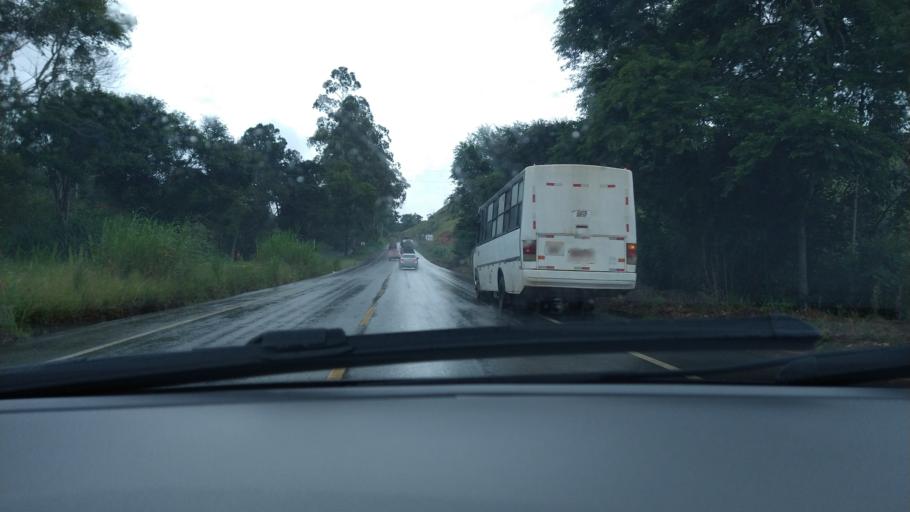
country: BR
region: Minas Gerais
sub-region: Vicosa
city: Vicosa
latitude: -20.6214
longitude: -42.8686
